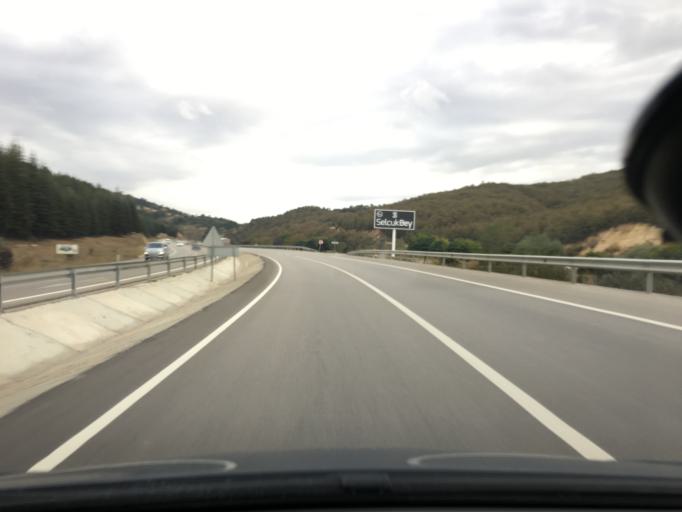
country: TR
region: Afyonkarahisar
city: Sincanli
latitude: 38.7071
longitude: 30.3180
